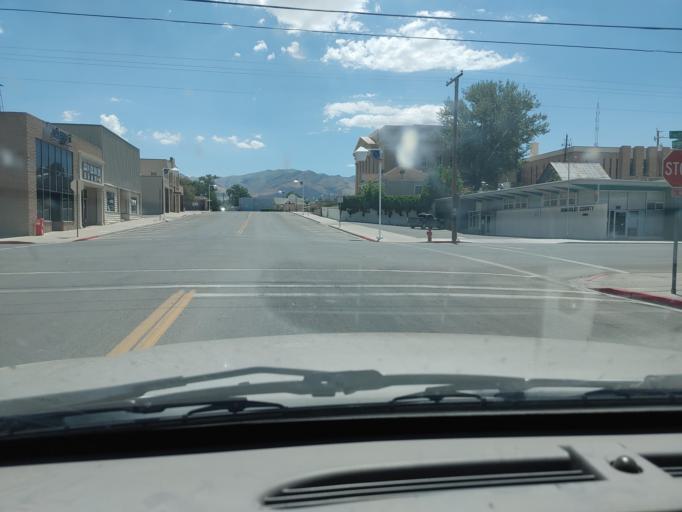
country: US
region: Nevada
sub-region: Humboldt County
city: Winnemucca
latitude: 40.9730
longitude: -117.7340
